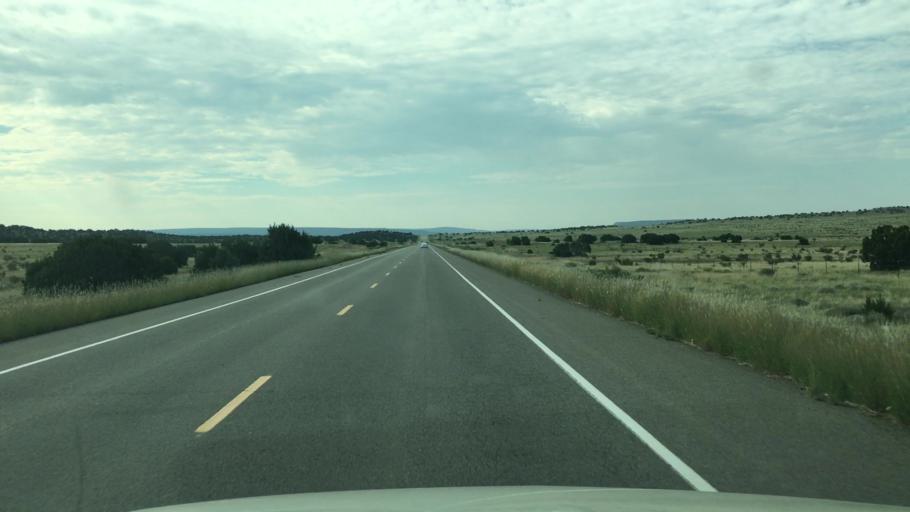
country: US
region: New Mexico
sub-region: Santa Fe County
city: Eldorado at Santa Fe
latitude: 35.4443
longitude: -105.8869
